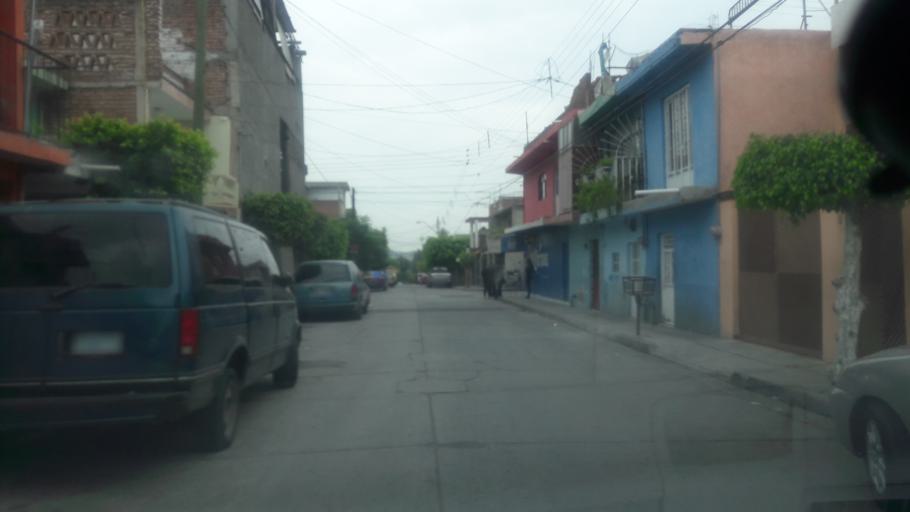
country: MX
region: Guanajuato
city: Leon
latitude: 21.1407
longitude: -101.6968
